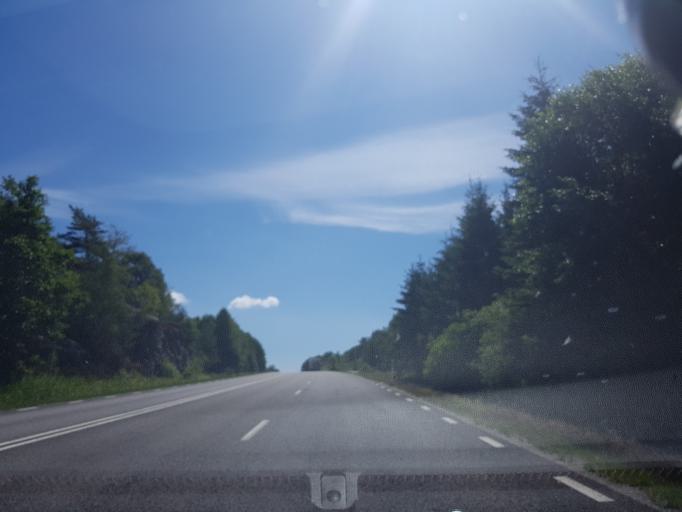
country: SE
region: Vaestra Goetaland
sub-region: Lysekils Kommun
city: Lysekil
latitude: 58.1614
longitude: 11.4922
